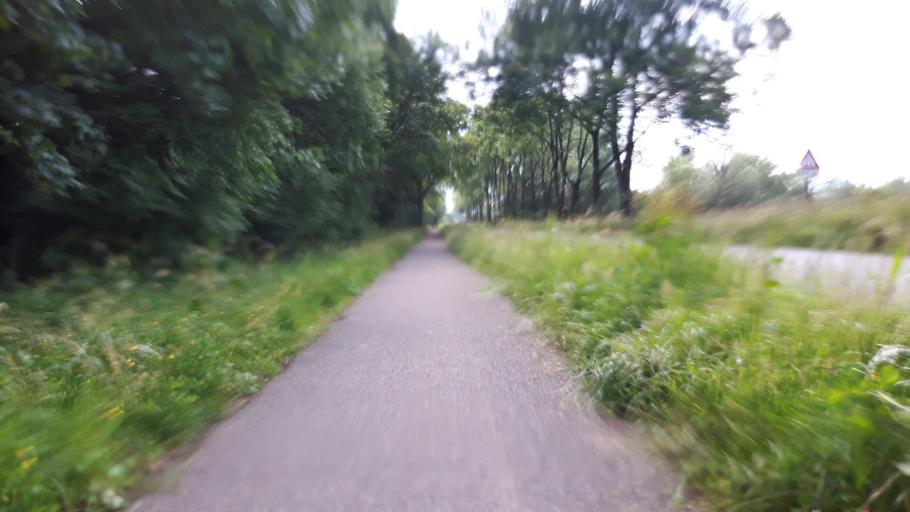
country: NL
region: Utrecht
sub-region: Gemeente Montfoort
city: Montfoort
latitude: 52.1021
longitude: 4.9627
